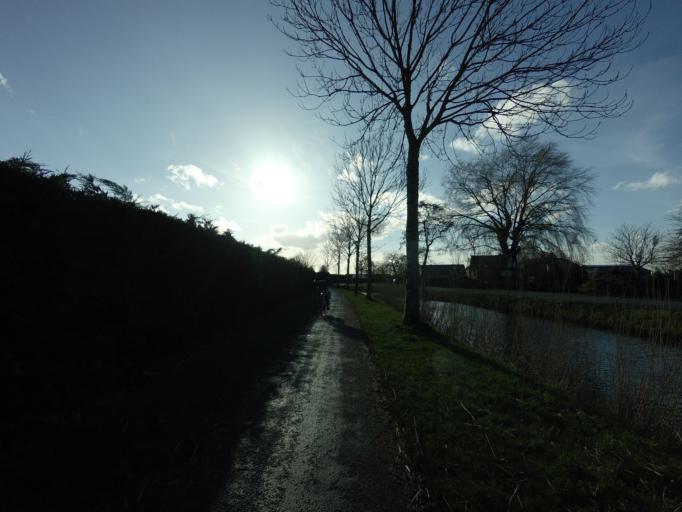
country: NL
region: Utrecht
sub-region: Gemeente IJsselstein
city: IJsselstein
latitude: 51.9895
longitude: 5.0419
